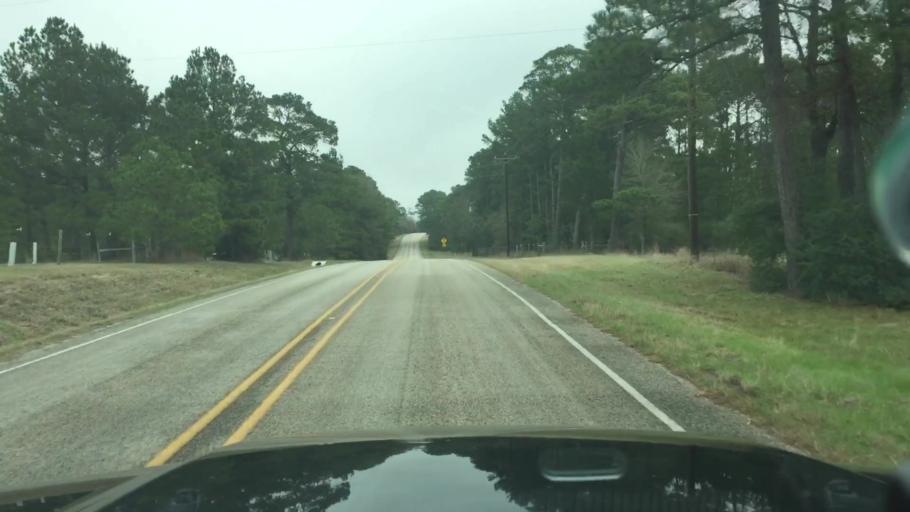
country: US
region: Texas
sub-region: Fayette County
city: La Grange
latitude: 30.0113
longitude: -96.9372
